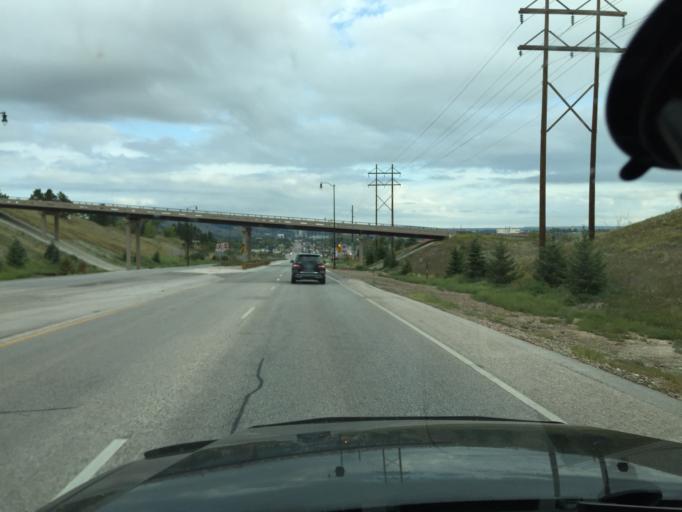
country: US
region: South Dakota
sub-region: Pennington County
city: Rapid City
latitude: 44.0550
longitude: -103.2323
